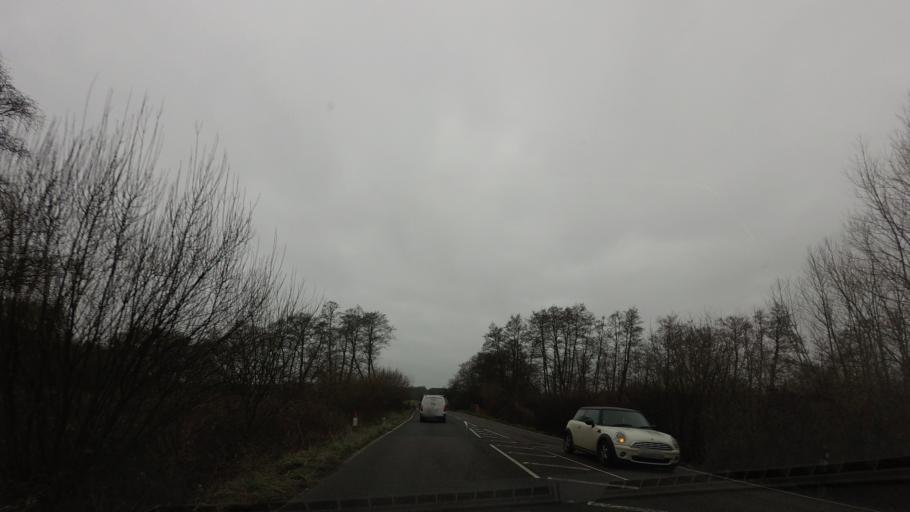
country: GB
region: England
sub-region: East Sussex
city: Battle
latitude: 50.9305
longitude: 0.5251
